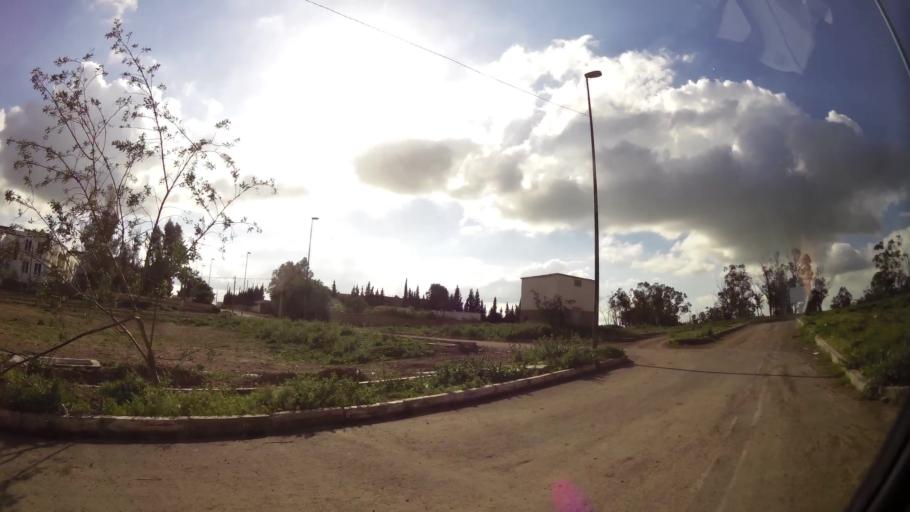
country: MA
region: Chaouia-Ouardigha
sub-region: Settat Province
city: Settat
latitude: 33.0123
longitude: -7.6360
